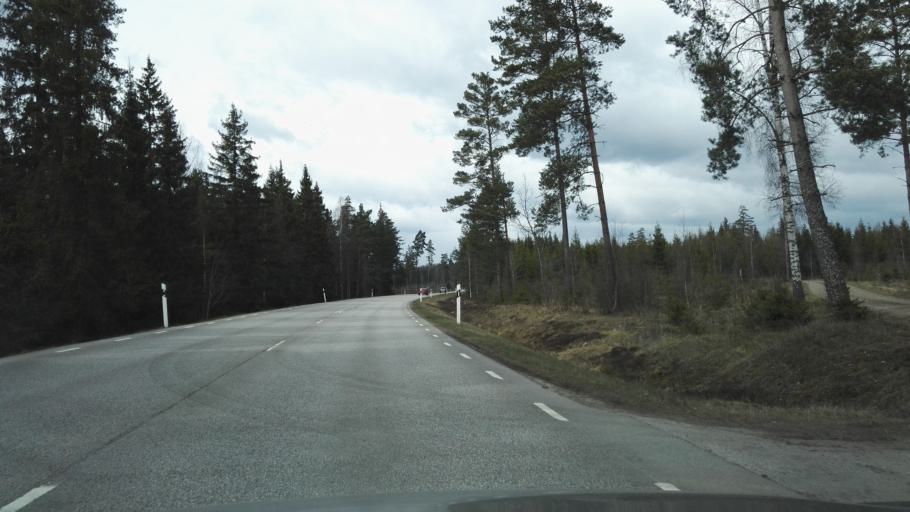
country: SE
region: Kronoberg
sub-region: Vaxjo Kommun
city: Braas
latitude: 57.0400
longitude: 15.0660
